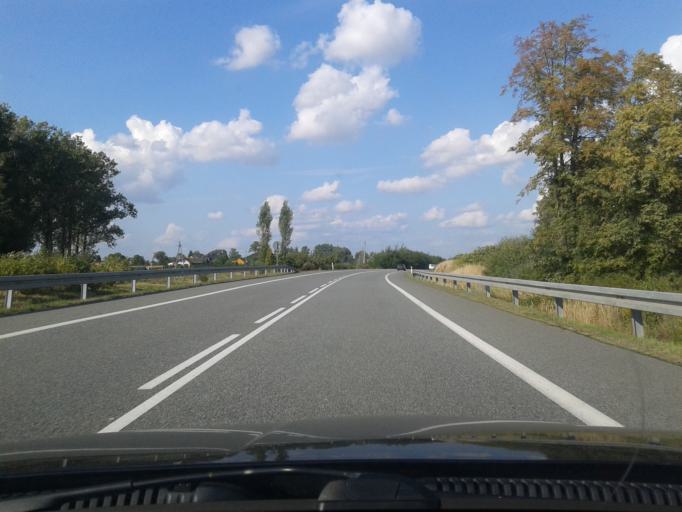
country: PL
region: Silesian Voivodeship
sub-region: Powiat raciborski
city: Chalupki
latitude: 49.9333
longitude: 18.3252
